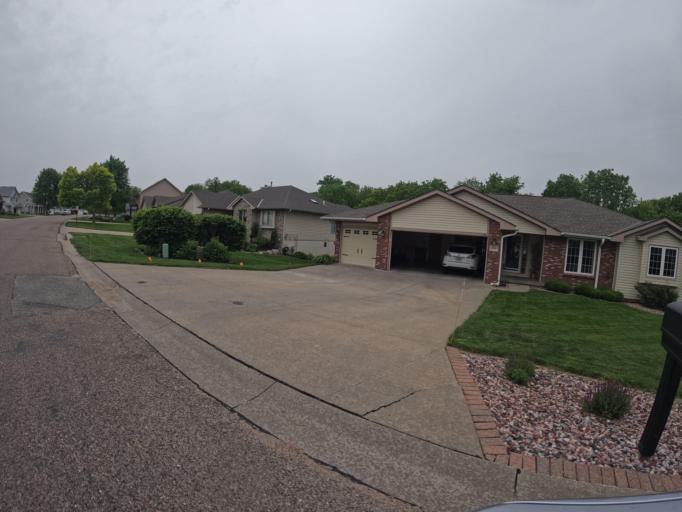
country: US
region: Nebraska
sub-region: Sarpy County
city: Offutt Air Force Base
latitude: 41.0476
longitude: -95.9745
